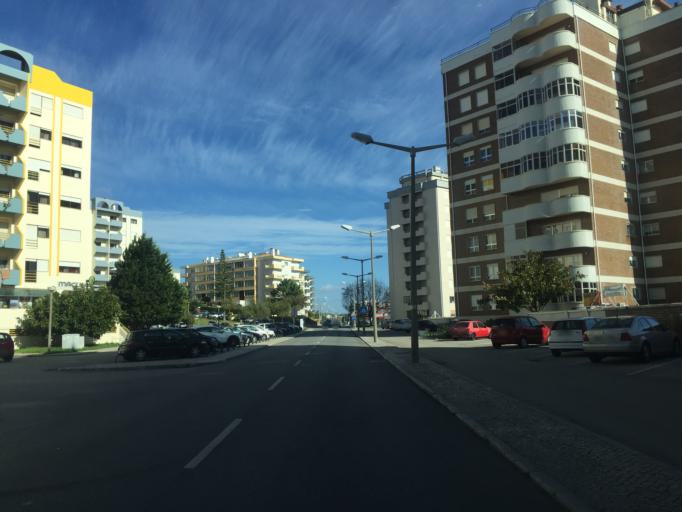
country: PT
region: Coimbra
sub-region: Figueira da Foz
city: Figueira da Foz
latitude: 40.1634
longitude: -8.8631
